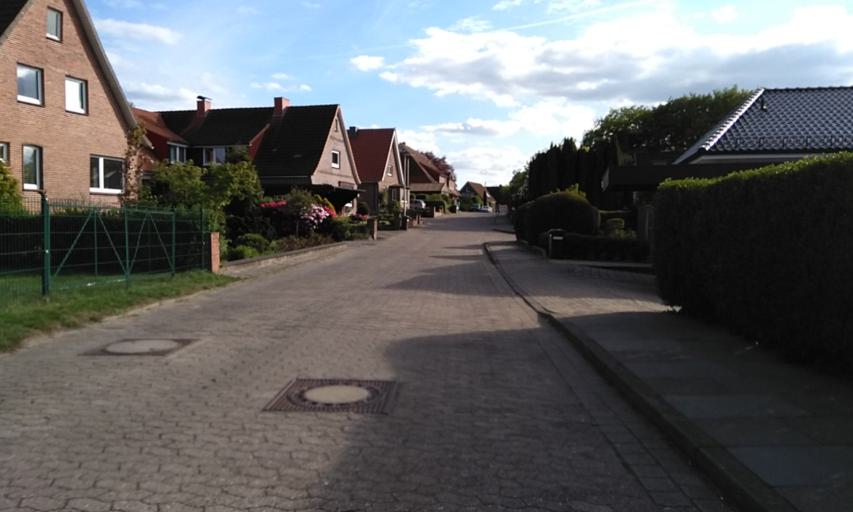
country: DE
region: Lower Saxony
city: Nottensdorf
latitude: 53.4822
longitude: 9.6184
